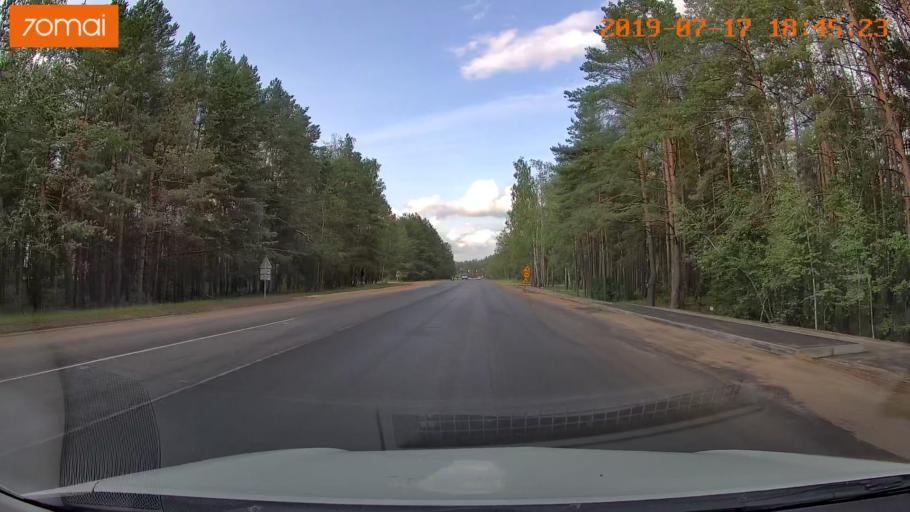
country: BY
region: Mogilev
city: Asipovichy
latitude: 53.3244
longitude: 28.6541
